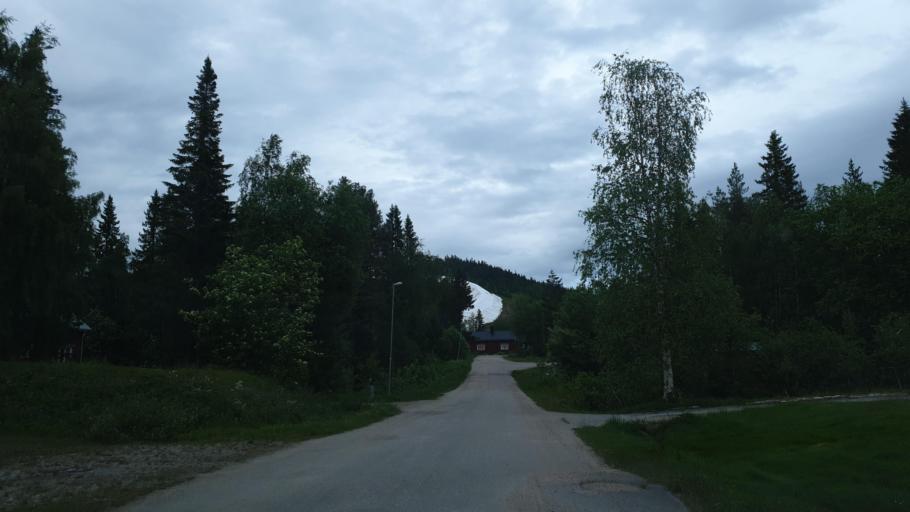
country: SE
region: Norrbotten
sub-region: Jokkmokks Kommun
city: Jokkmokk
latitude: 66.1526
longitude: 19.9838
